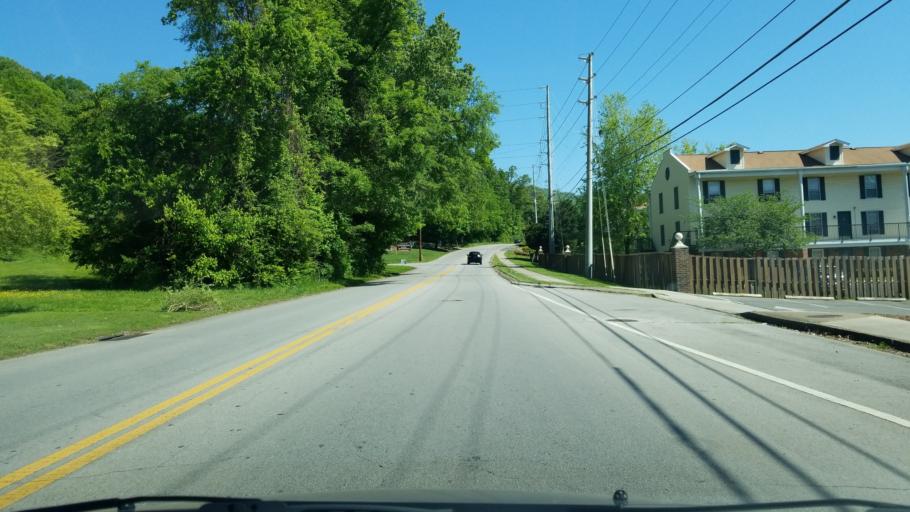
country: US
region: Tennessee
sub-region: Hamilton County
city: Signal Mountain
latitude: 35.1020
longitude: -85.3275
